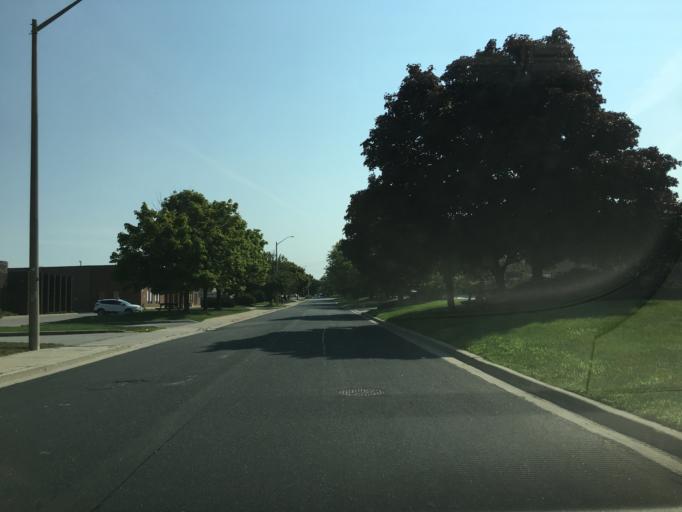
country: CA
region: Ontario
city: Markham
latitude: 43.8246
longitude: -79.3304
